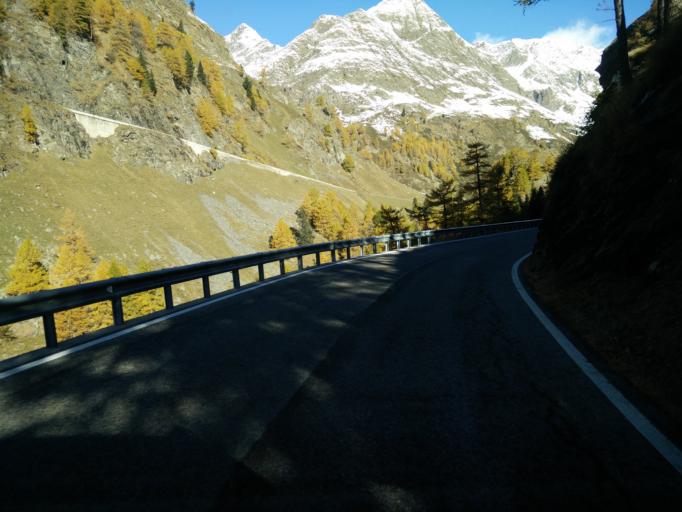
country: IT
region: Trentino-Alto Adige
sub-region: Bolzano
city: Moso in Passiria
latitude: 46.8909
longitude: 11.1309
